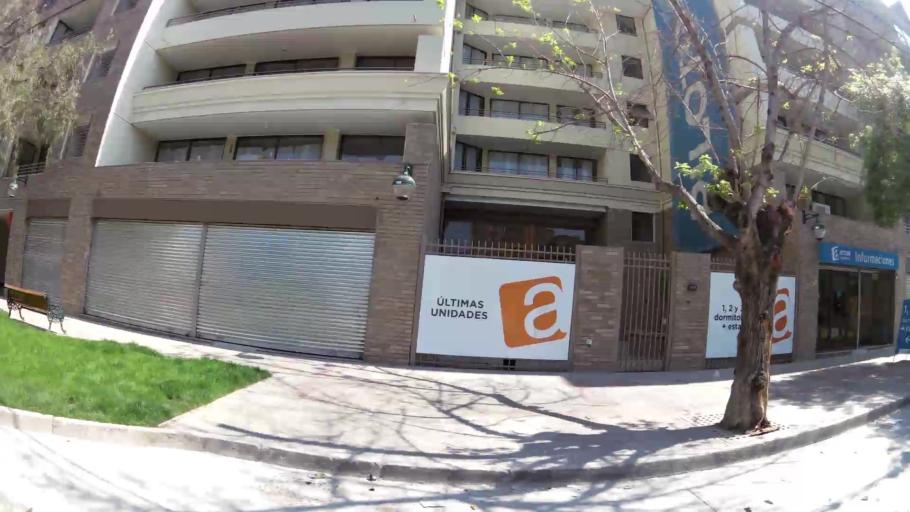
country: CL
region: Santiago Metropolitan
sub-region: Provincia de Santiago
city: Santiago
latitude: -33.4514
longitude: -70.6246
